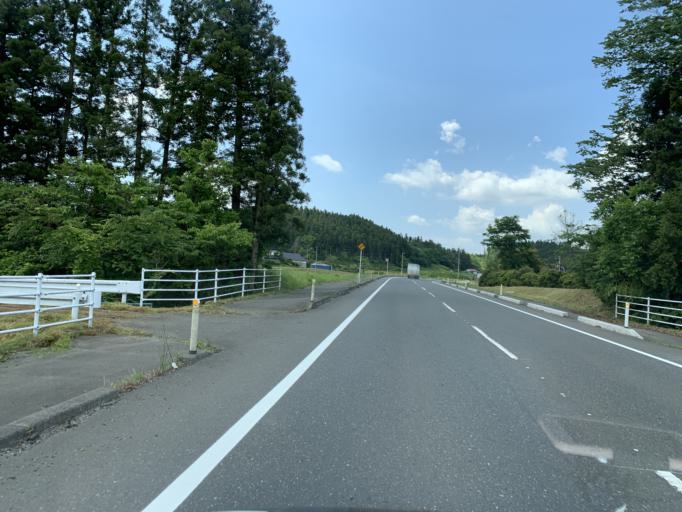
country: JP
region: Miyagi
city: Furukawa
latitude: 38.7317
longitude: 140.9579
